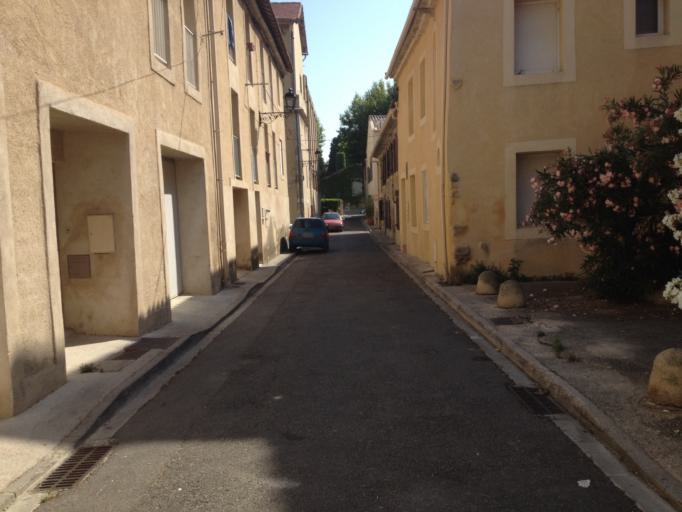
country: FR
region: Provence-Alpes-Cote d'Azur
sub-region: Departement du Vaucluse
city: Courthezon
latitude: 44.0881
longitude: 4.8850
